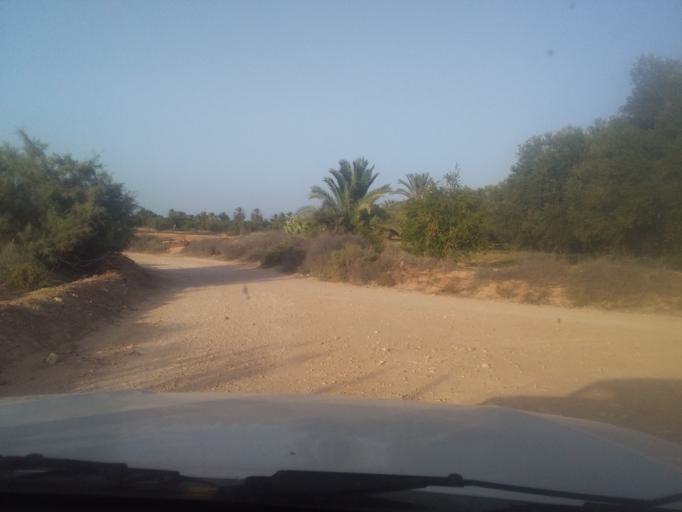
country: TN
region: Qabis
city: Gabes
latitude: 33.6326
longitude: 10.2931
